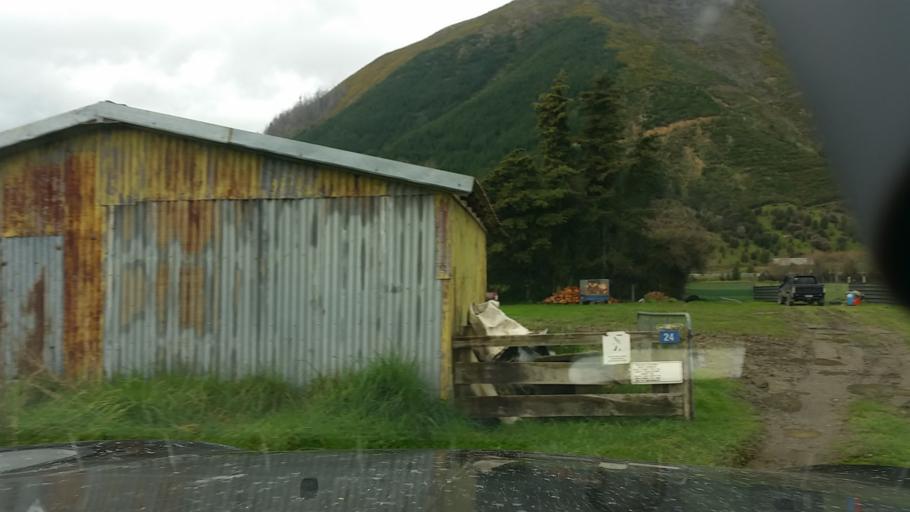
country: NZ
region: Marlborough
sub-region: Marlborough District
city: Picton
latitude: -41.2890
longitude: 173.6716
